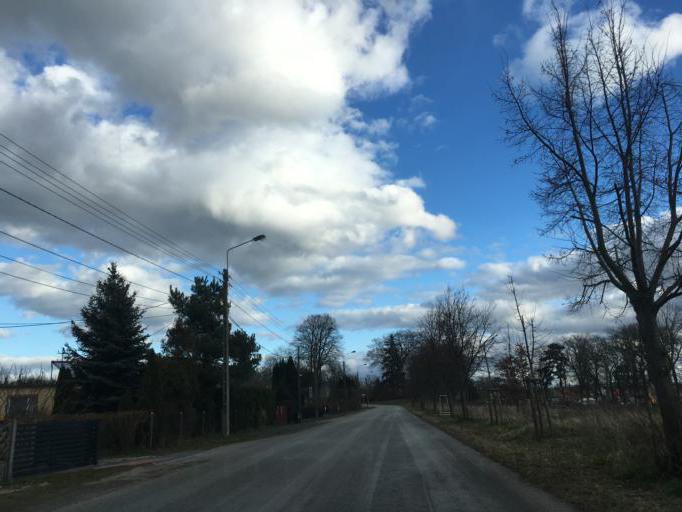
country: PL
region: Pomeranian Voivodeship
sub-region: Powiat gdanski
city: Cedry Wielkie
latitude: 54.3107
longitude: 18.9197
